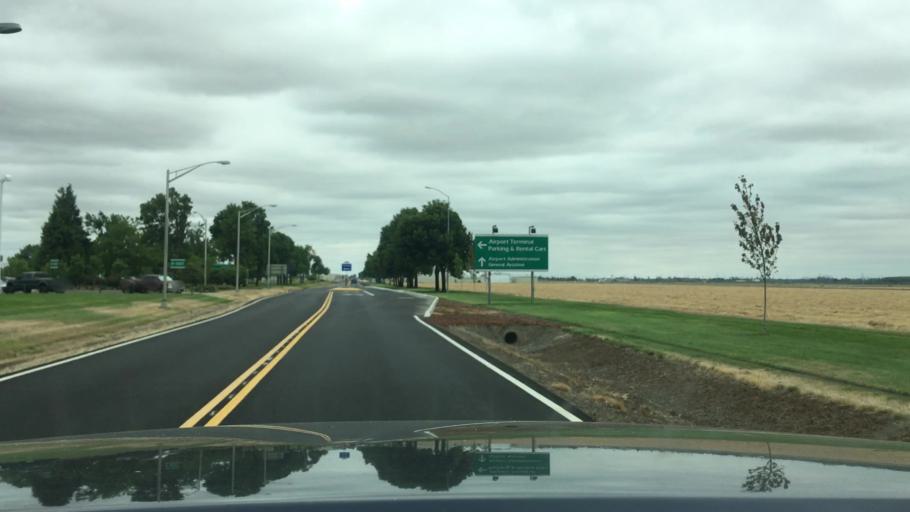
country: US
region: Oregon
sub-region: Lane County
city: Junction City
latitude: 44.1167
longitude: -123.2084
